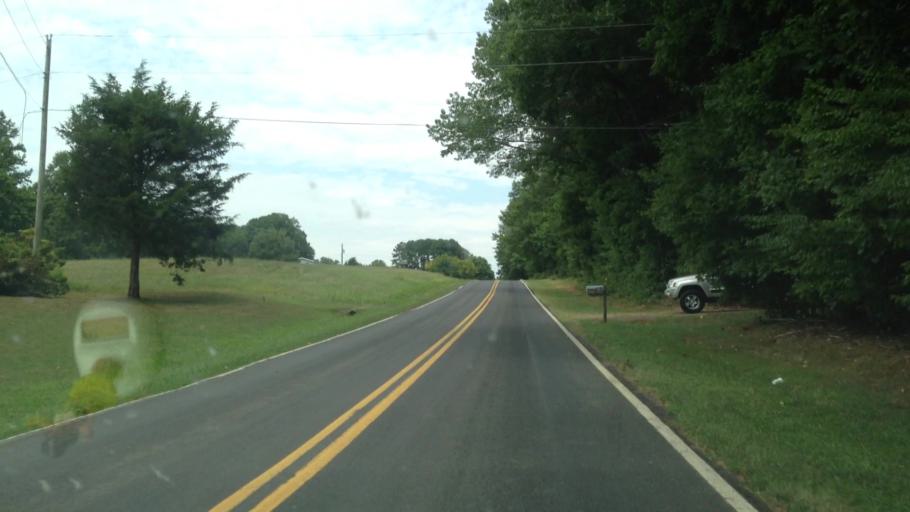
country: US
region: North Carolina
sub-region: Forsyth County
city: Walkertown
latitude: 36.2187
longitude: -80.1148
